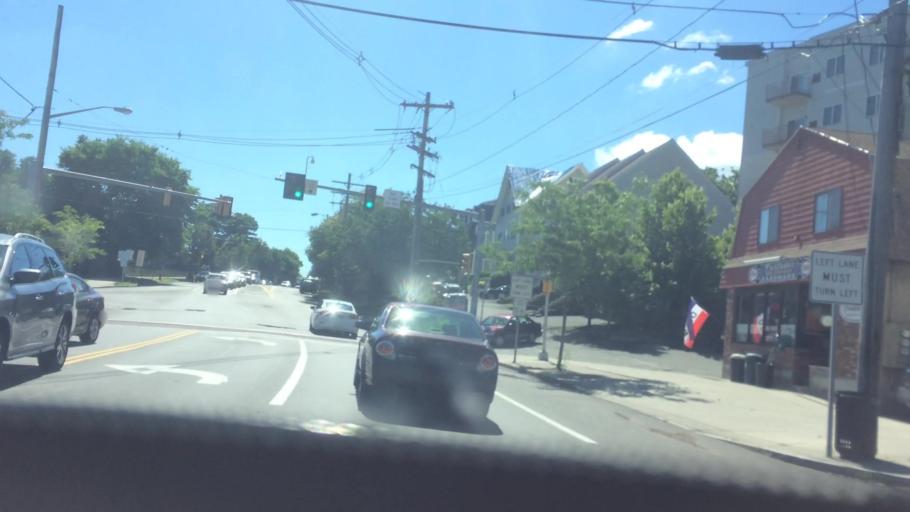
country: US
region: Massachusetts
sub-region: Essex County
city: Peabody
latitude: 42.5229
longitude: -70.9201
